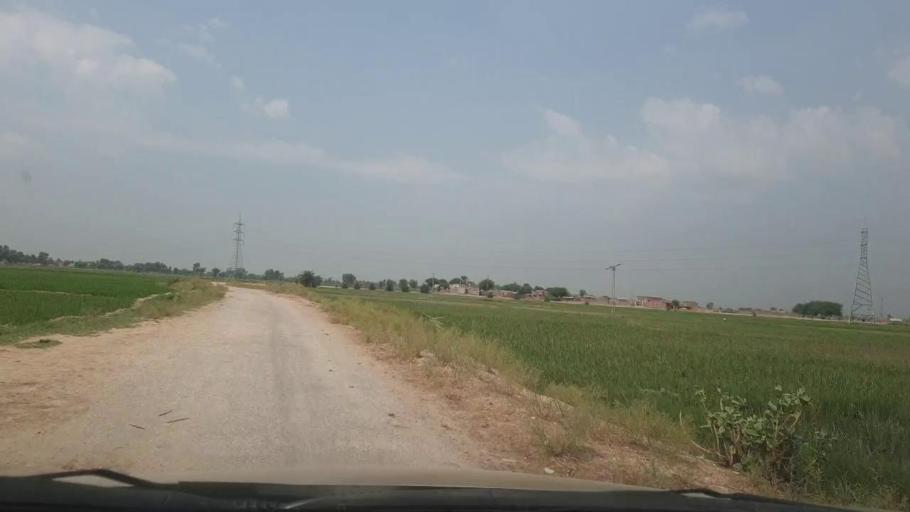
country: PK
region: Sindh
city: Ratodero
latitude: 27.6957
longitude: 68.2540
